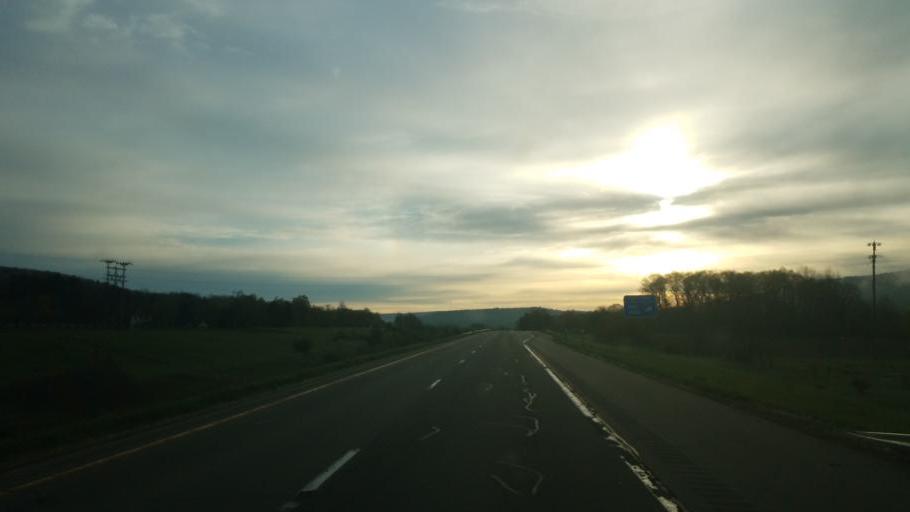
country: US
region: New York
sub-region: Allegany County
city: Friendship
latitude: 42.2225
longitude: -78.1068
